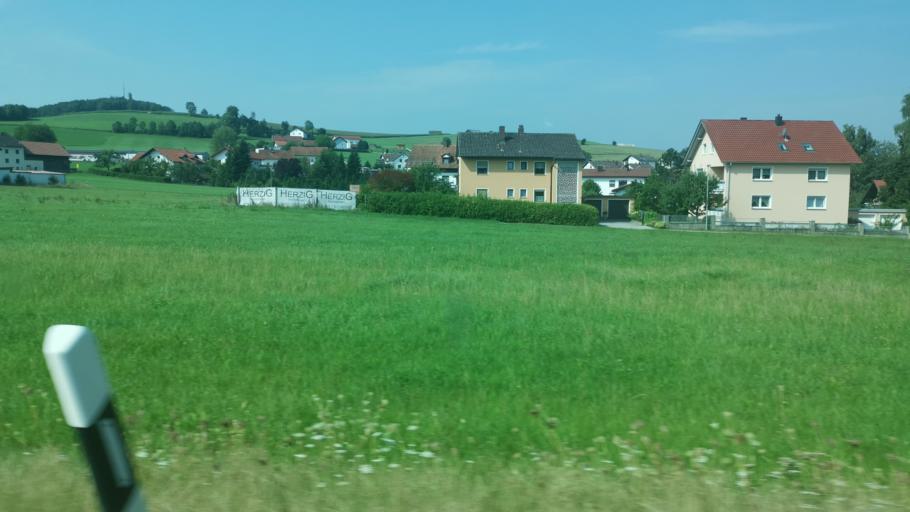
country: DE
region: Bavaria
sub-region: Upper Palatinate
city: Willmering
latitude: 49.2391
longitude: 12.6753
